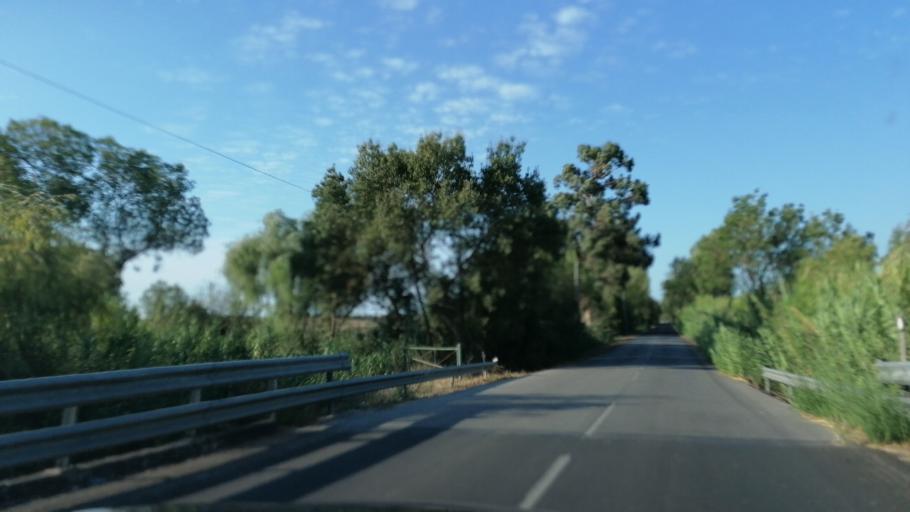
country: PT
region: Santarem
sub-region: Santarem
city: Santarem
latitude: 39.2648
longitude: -8.6647
